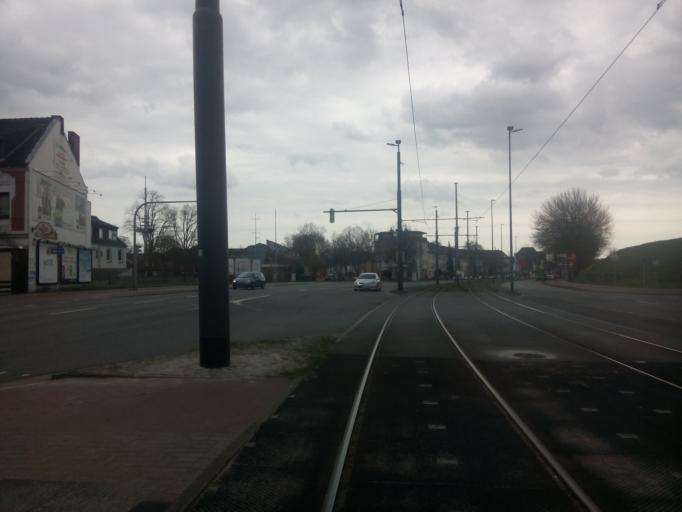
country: DE
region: Bremen
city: Bremen
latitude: 53.1015
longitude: 8.7740
